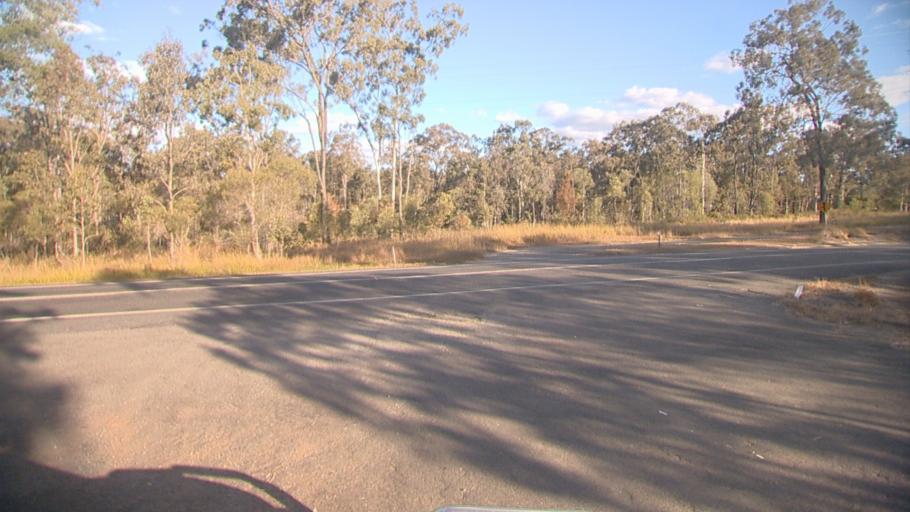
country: AU
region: Queensland
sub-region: Logan
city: Chambers Flat
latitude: -27.8033
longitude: 153.0817
